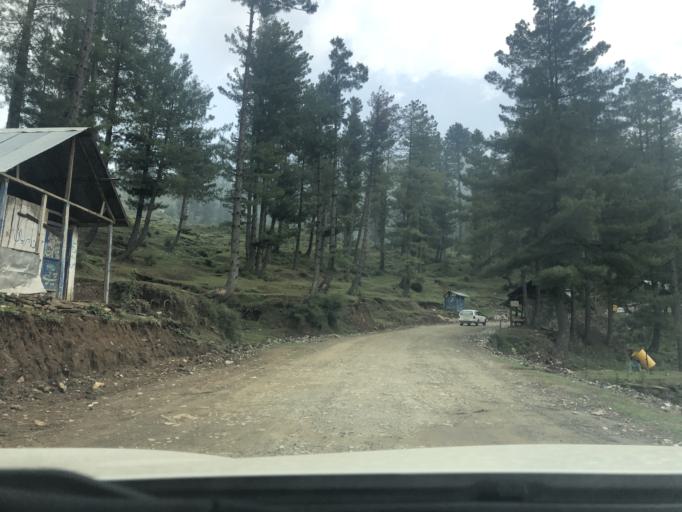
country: PK
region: Khyber Pakhtunkhwa
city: Alpurai
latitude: 34.8171
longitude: 72.5740
